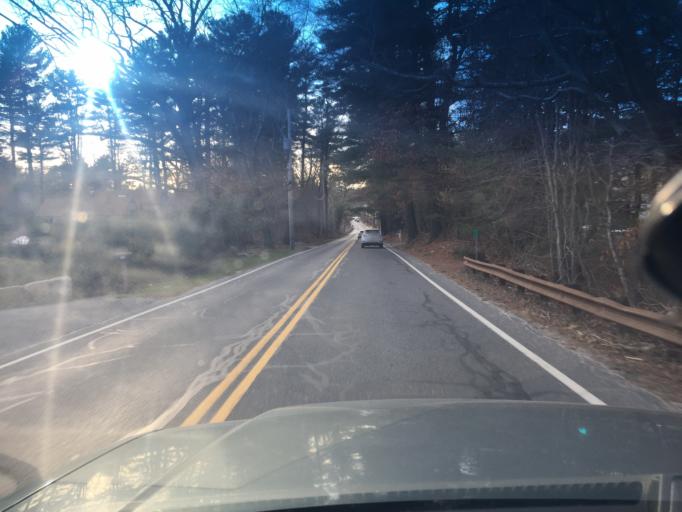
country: US
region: Massachusetts
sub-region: Middlesex County
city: Holliston
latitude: 42.2200
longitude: -71.4051
